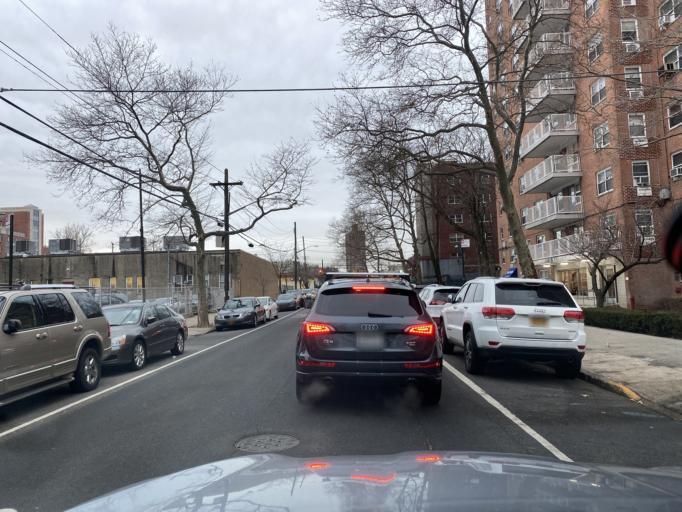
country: US
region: New York
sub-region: New York County
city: Inwood
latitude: 40.8817
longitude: -73.9076
